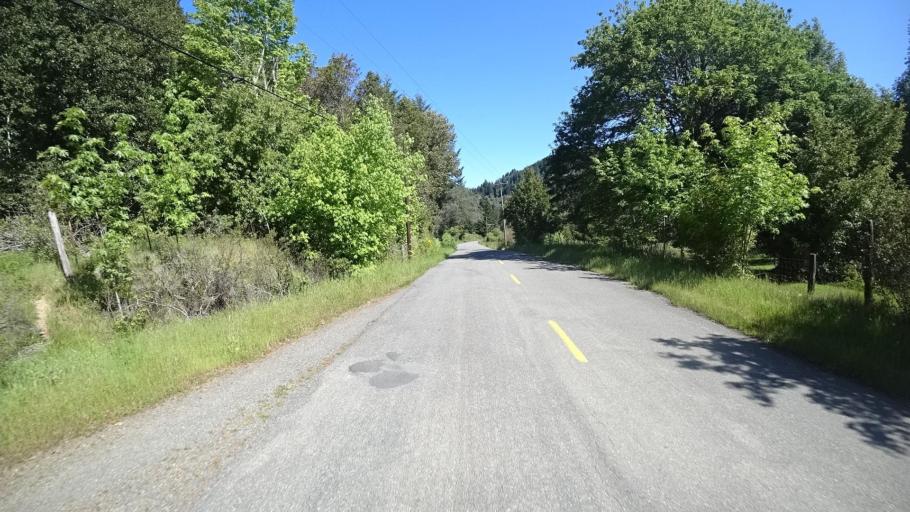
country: US
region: California
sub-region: Humboldt County
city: Rio Dell
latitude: 40.2632
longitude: -124.1968
